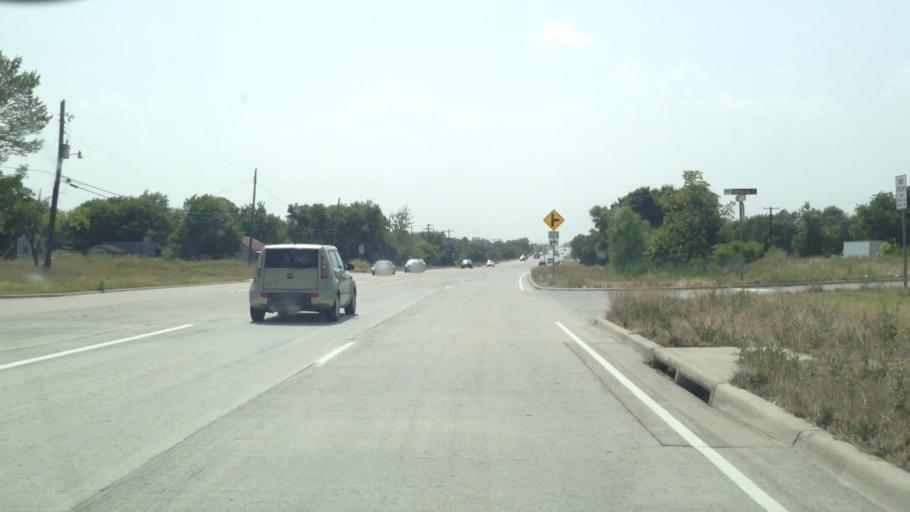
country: US
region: Texas
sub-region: Collin County
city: Farmersville
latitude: 33.1566
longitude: -96.3647
